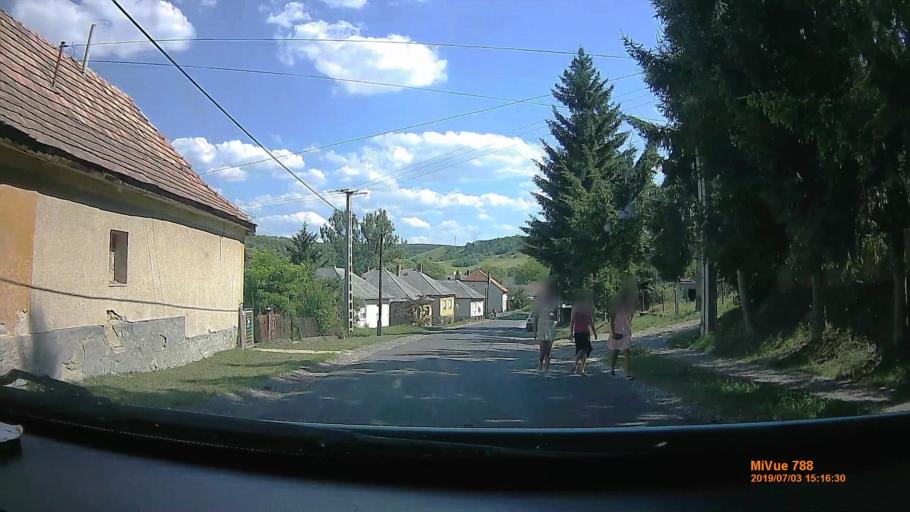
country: HU
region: Borsod-Abauj-Zemplen
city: Farkaslyuk
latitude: 48.2103
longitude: 20.3981
